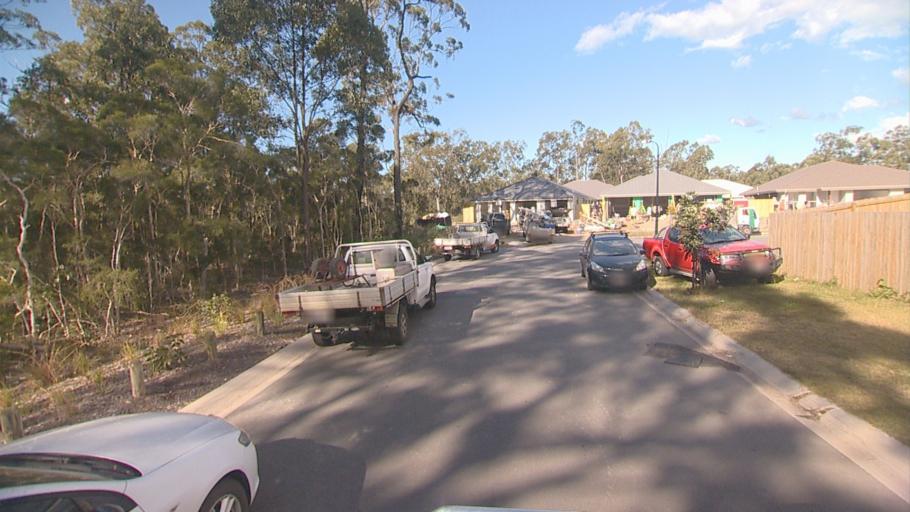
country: AU
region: Queensland
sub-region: Logan
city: Logan Reserve
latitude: -27.6929
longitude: 153.0972
